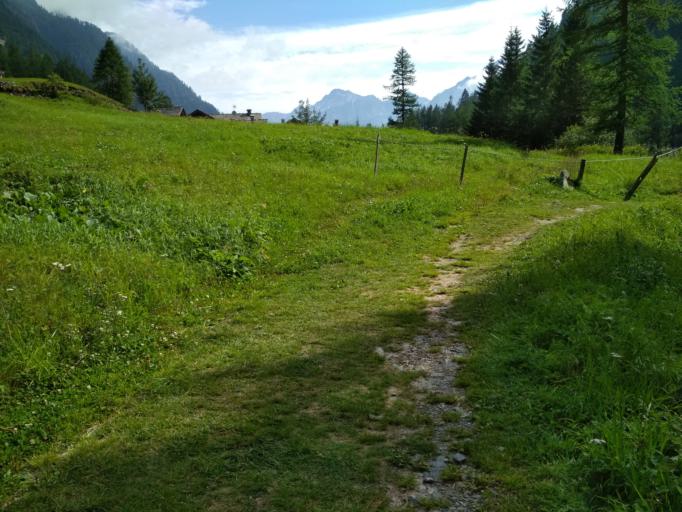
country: IT
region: Aosta Valley
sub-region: Valle d'Aosta
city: Gressoney-La-Trinite
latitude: 45.8209
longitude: 7.8254
